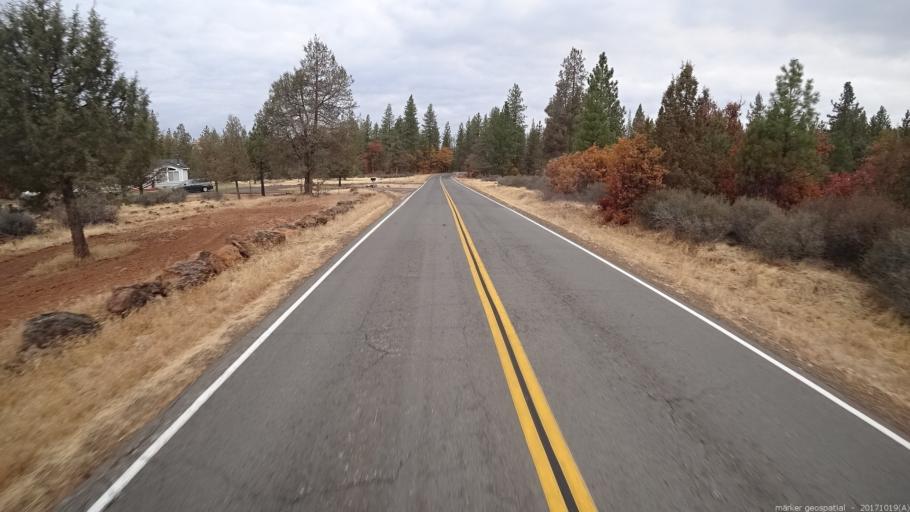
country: US
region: California
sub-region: Shasta County
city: Burney
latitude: 41.1322
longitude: -121.3418
